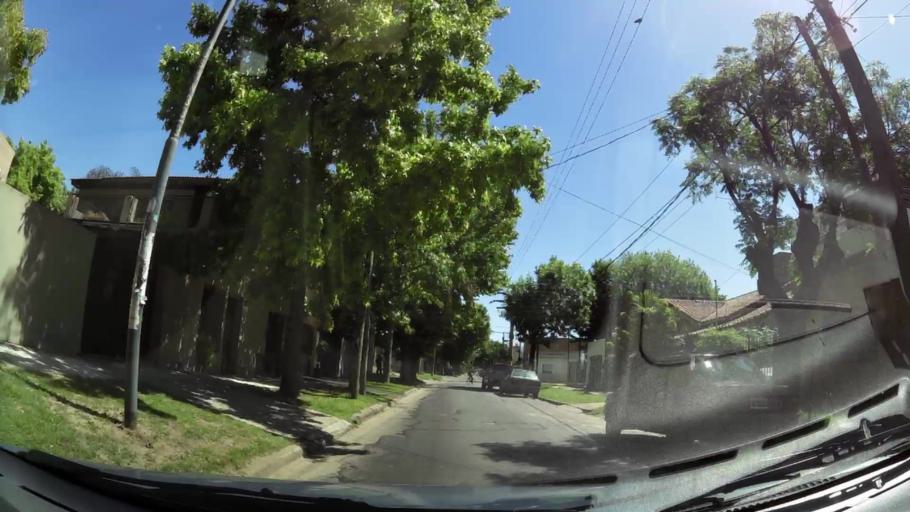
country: AR
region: Buenos Aires
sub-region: Partido de General San Martin
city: General San Martin
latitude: -34.5590
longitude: -58.5542
